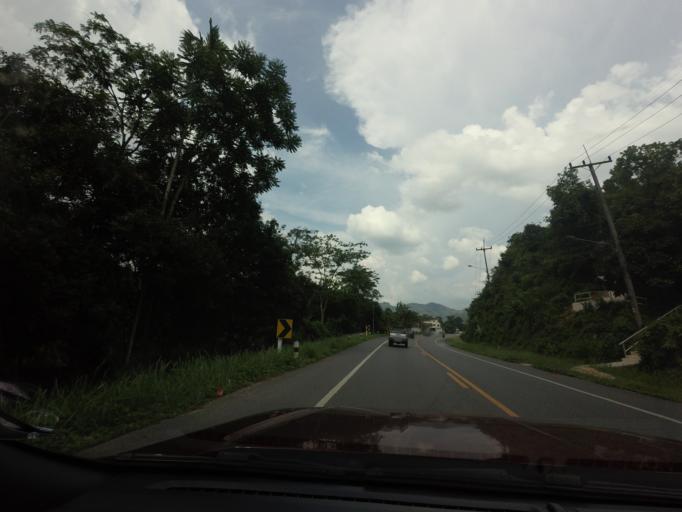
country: TH
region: Yala
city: Ban Nang Sata
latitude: 6.2657
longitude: 101.2703
